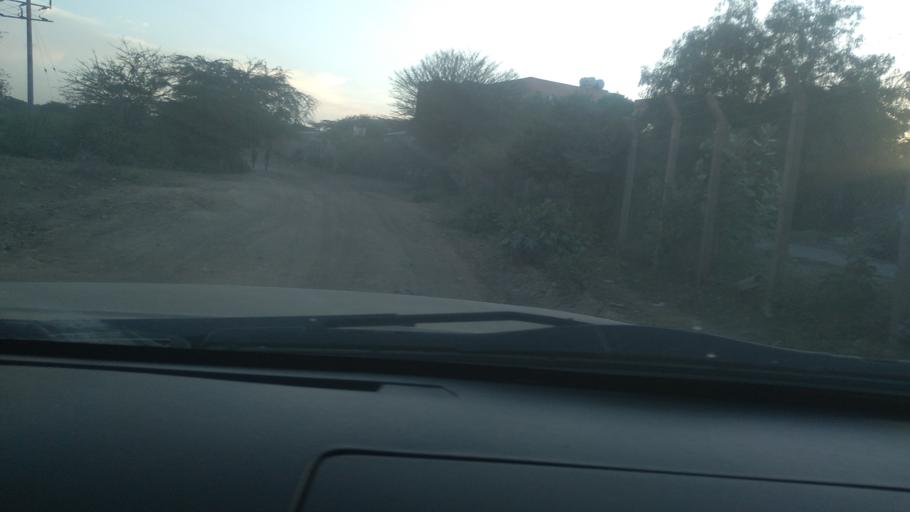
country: ET
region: Oromiya
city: Asbe Teferi
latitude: 9.2386
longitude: 40.7622
